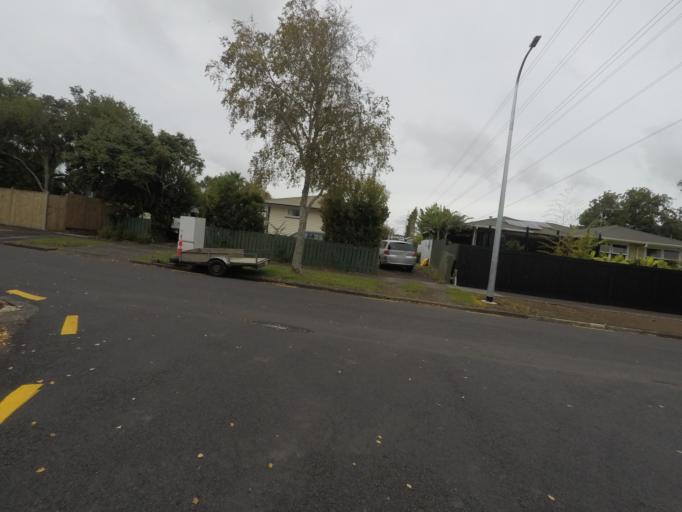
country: NZ
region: Auckland
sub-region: Auckland
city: Rosebank
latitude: -36.8933
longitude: 174.6769
